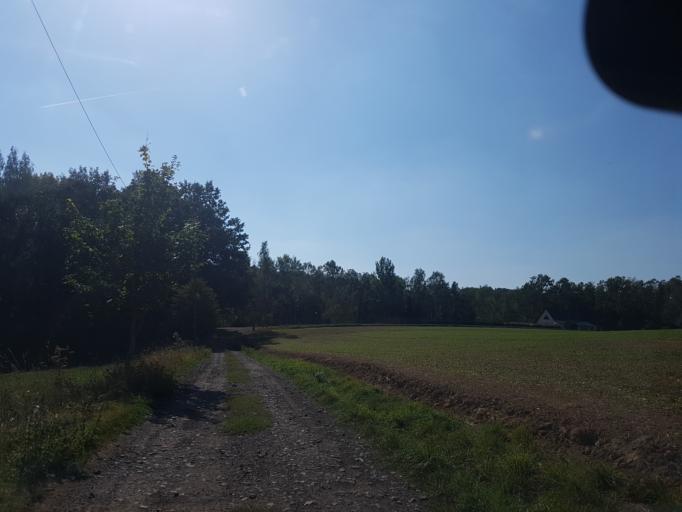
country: DE
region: Saxony
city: Kriebstein
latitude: 51.0525
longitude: 13.0006
